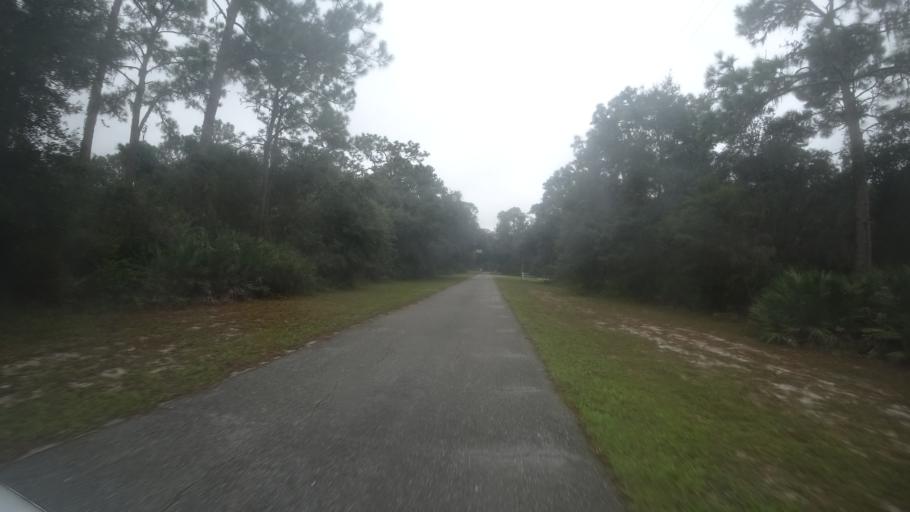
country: US
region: Florida
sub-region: Sarasota County
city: The Meadows
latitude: 27.3968
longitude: -82.3285
